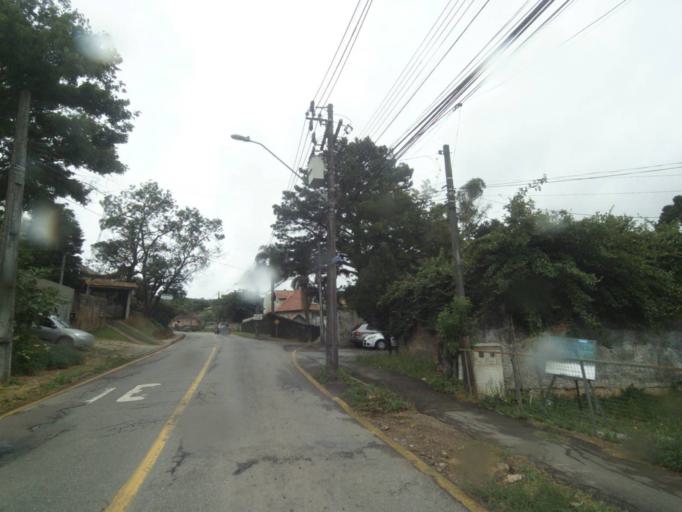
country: BR
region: Parana
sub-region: Curitiba
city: Curitiba
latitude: -25.4286
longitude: -49.3249
